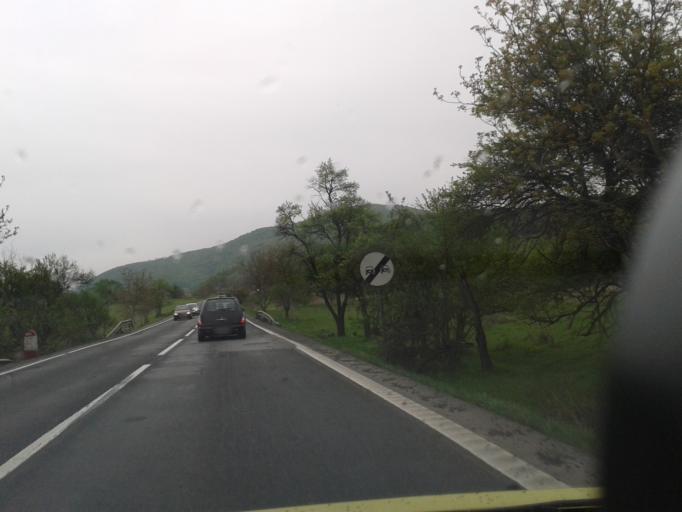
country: RO
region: Hunedoara
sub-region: Comuna Branisca
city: Branisca
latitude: 45.9189
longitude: 22.7211
